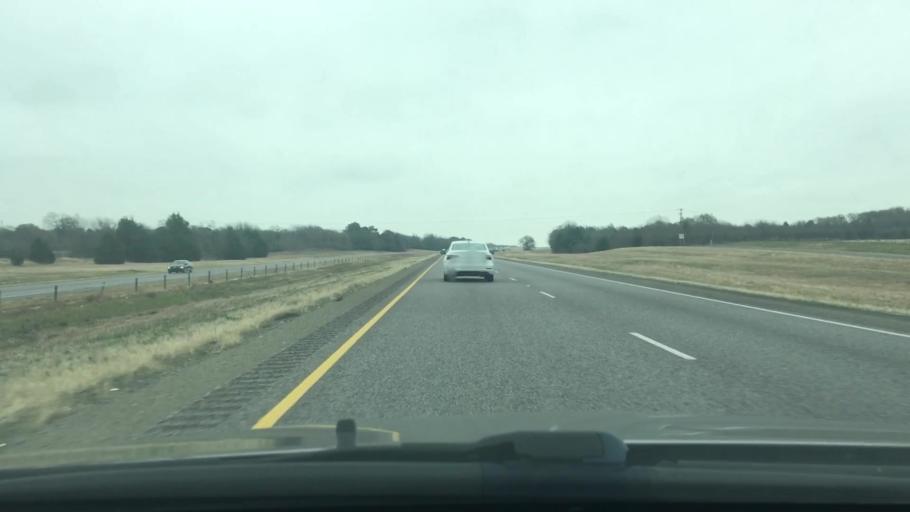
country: US
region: Texas
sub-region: Freestone County
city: Fairfield
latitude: 31.7816
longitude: -96.2344
